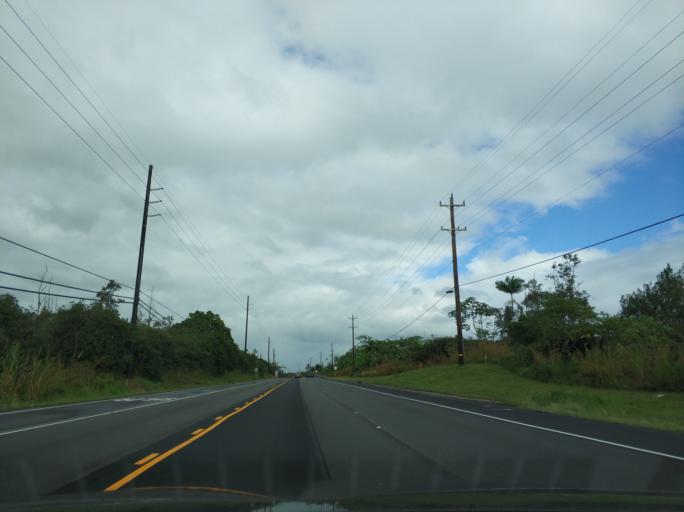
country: US
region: Hawaii
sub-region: Hawaii County
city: Orchidlands Estates
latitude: 19.5908
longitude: -155.0152
